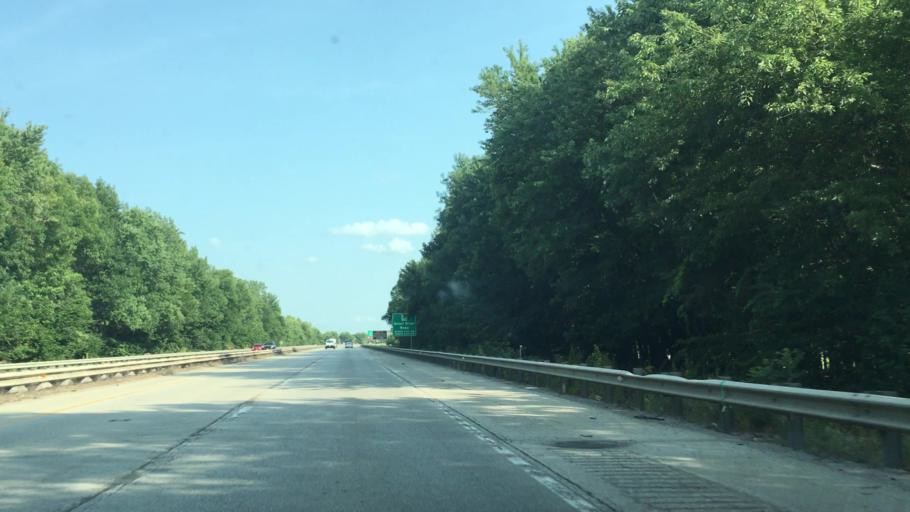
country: US
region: Illinois
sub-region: Rock Island County
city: Milan
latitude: 41.4720
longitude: -90.6234
